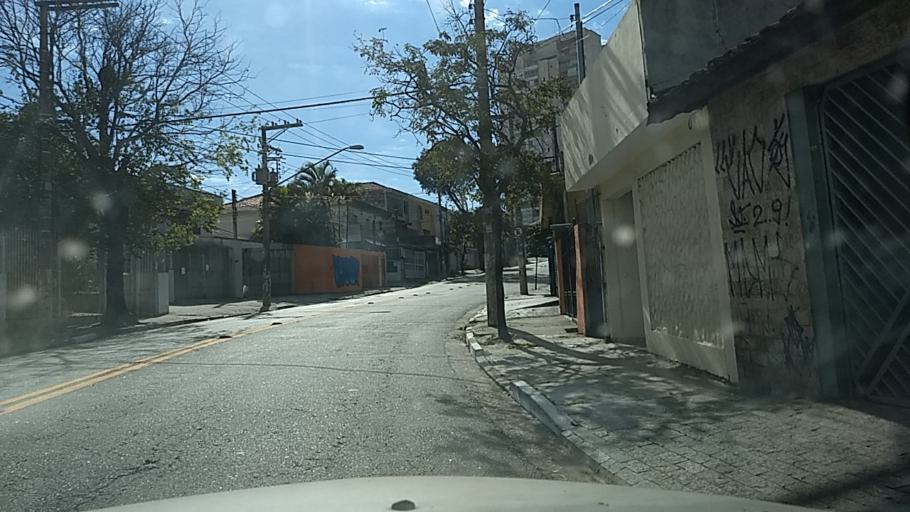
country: BR
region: Sao Paulo
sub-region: Sao Paulo
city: Sao Paulo
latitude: -23.4987
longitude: -46.5982
